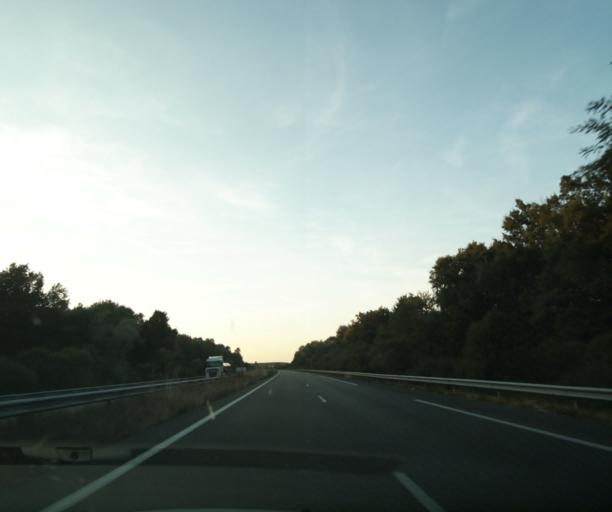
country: FR
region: Aquitaine
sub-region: Departement du Lot-et-Garonne
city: Fourques-sur-Garonne
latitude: 44.4170
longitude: 0.1757
